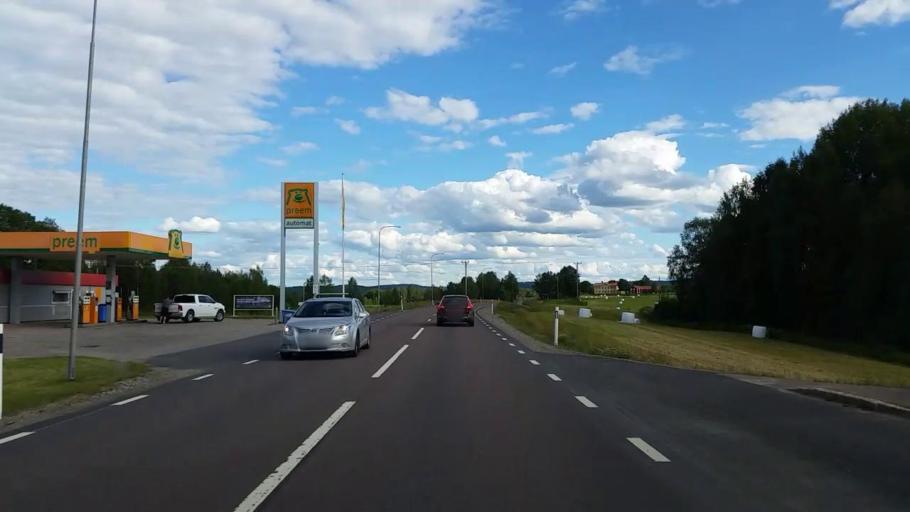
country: SE
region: Gaevleborg
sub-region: Ljusdals Kommun
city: Ljusdal
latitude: 61.8536
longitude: 15.9926
